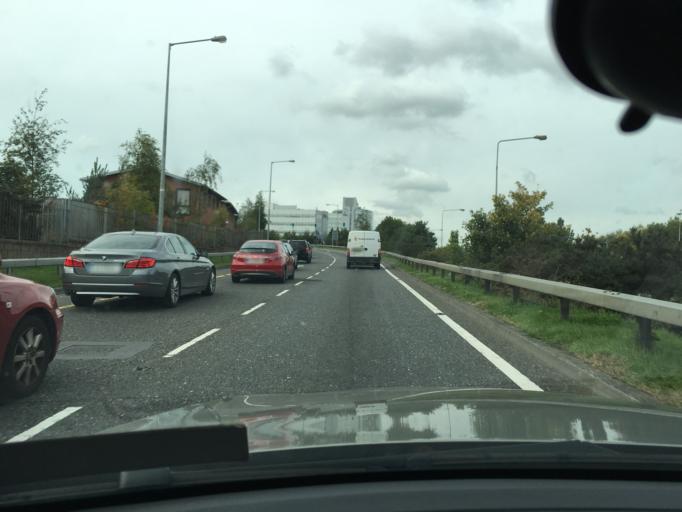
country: IE
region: Leinster
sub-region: Fingal County
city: Blanchardstown
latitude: 53.3907
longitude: -6.3796
